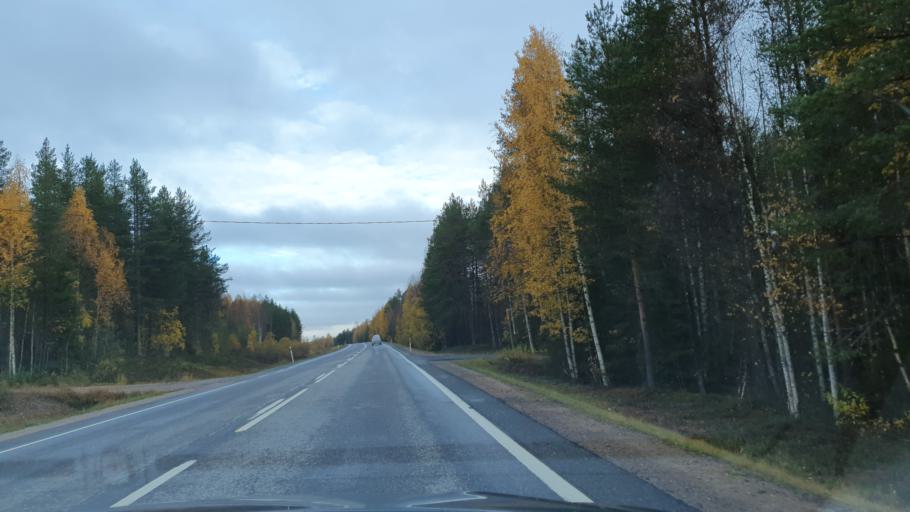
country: FI
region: Lapland
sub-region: Rovaniemi
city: Rovaniemi
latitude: 66.5862
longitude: 25.6149
